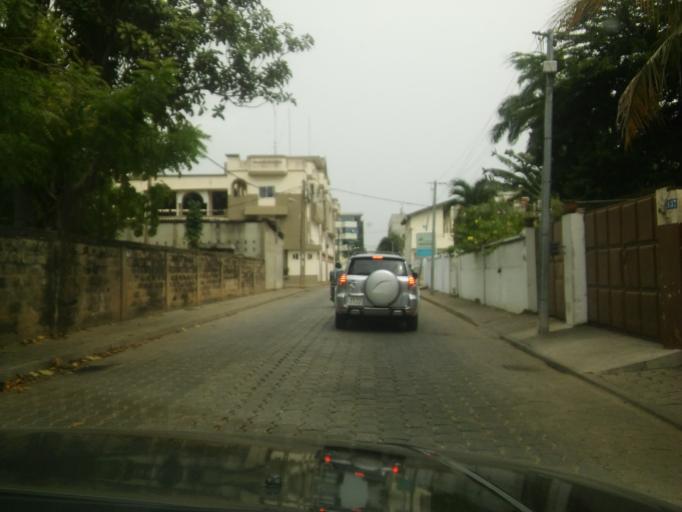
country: BJ
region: Littoral
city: Cotonou
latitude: 6.3563
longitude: 2.4202
